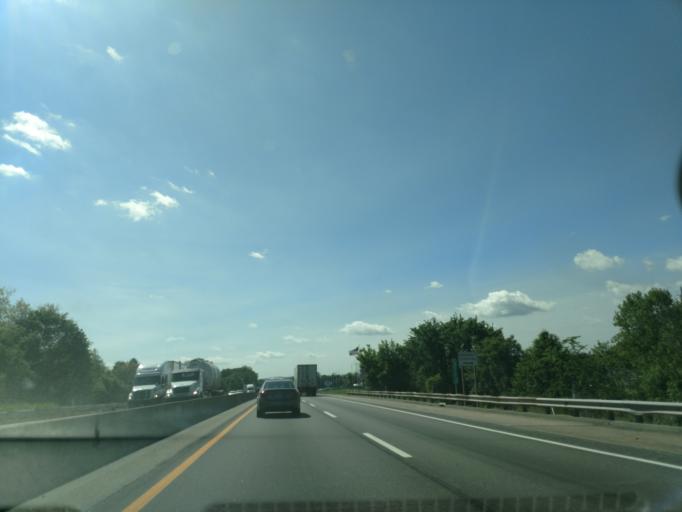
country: US
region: Pennsylvania
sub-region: Chester County
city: Downingtown
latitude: 40.0712
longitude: -75.6811
